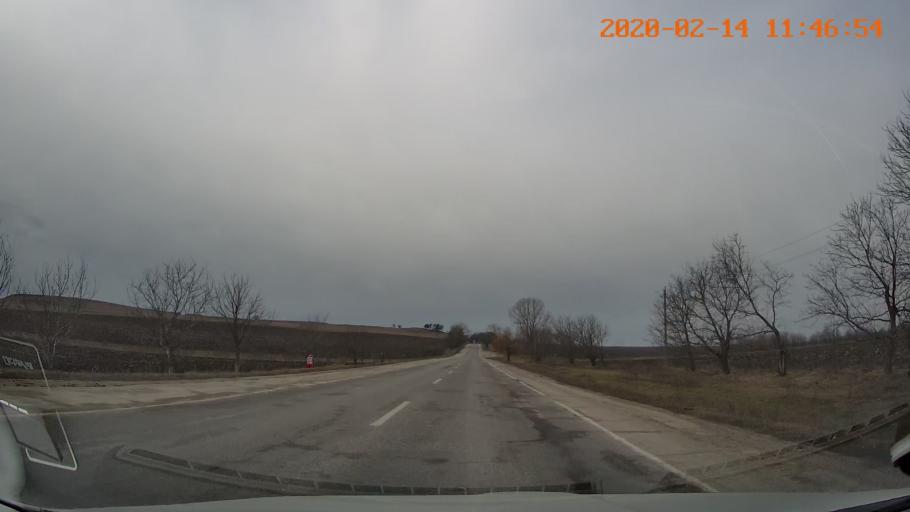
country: MD
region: Briceni
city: Briceni
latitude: 48.3165
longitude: 26.9819
